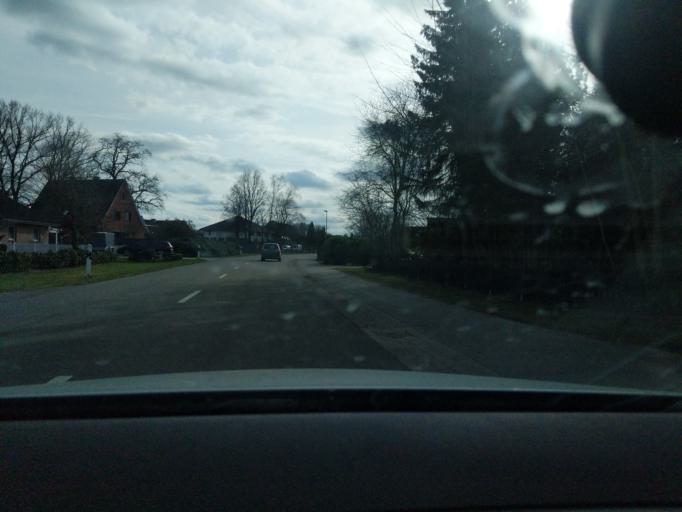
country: DE
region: Lower Saxony
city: Himmelpforten
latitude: 53.6315
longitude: 9.3214
